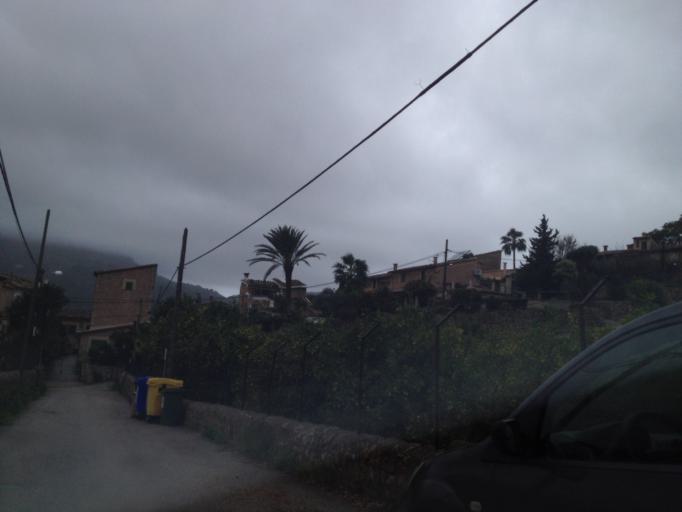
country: ES
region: Balearic Islands
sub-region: Illes Balears
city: Soller
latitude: 39.7736
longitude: 2.7202
